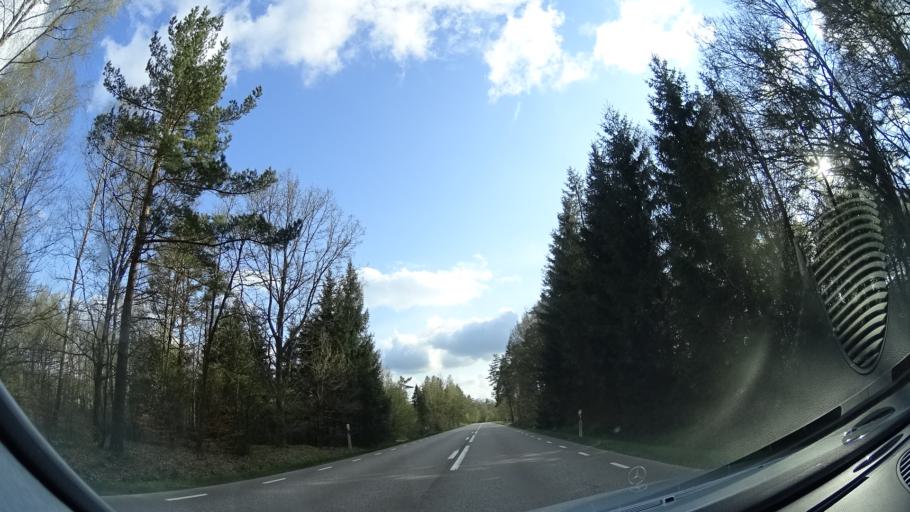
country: SE
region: Skane
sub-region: Perstorps Kommun
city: Perstorp
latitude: 56.1220
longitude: 13.3004
